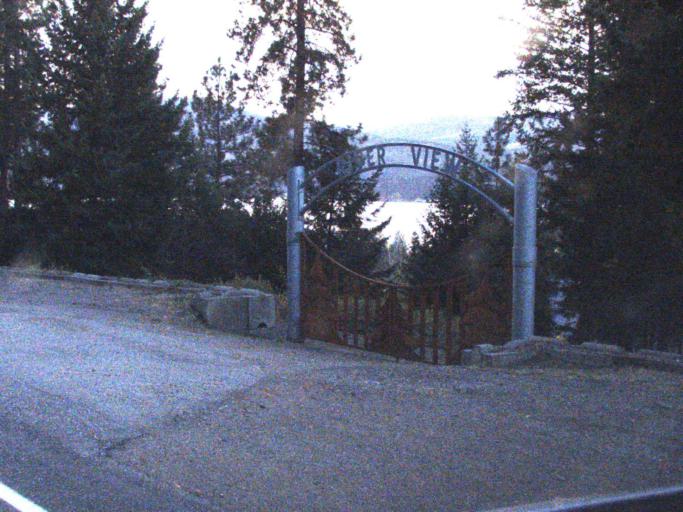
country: US
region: Washington
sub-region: Stevens County
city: Kettle Falls
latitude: 48.6688
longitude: -118.0407
